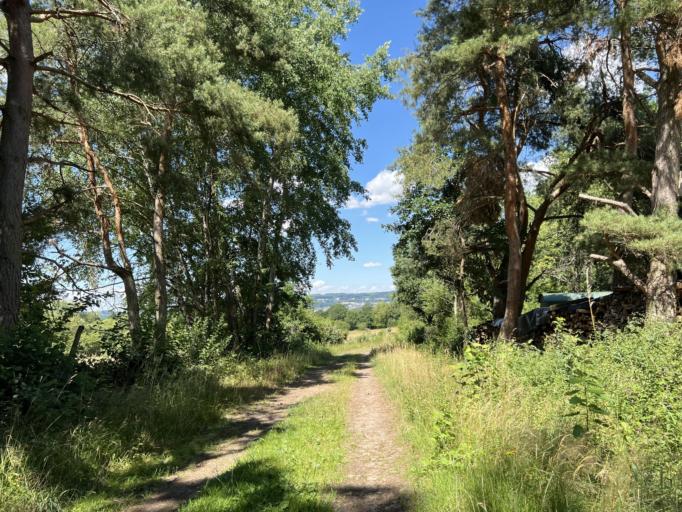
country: DE
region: Hesse
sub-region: Regierungsbezirk Darmstadt
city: Steinau an der Strasse
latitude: 50.3000
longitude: 9.4744
